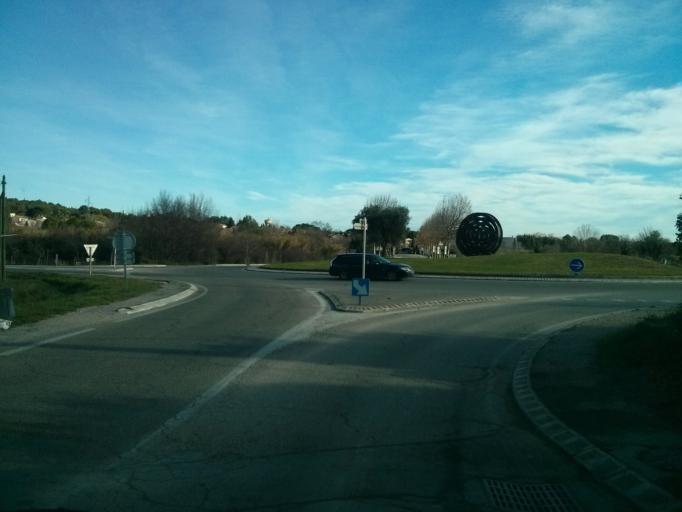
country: FR
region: Languedoc-Roussillon
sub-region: Departement du Gard
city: Mus
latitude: 43.7437
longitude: 4.2093
